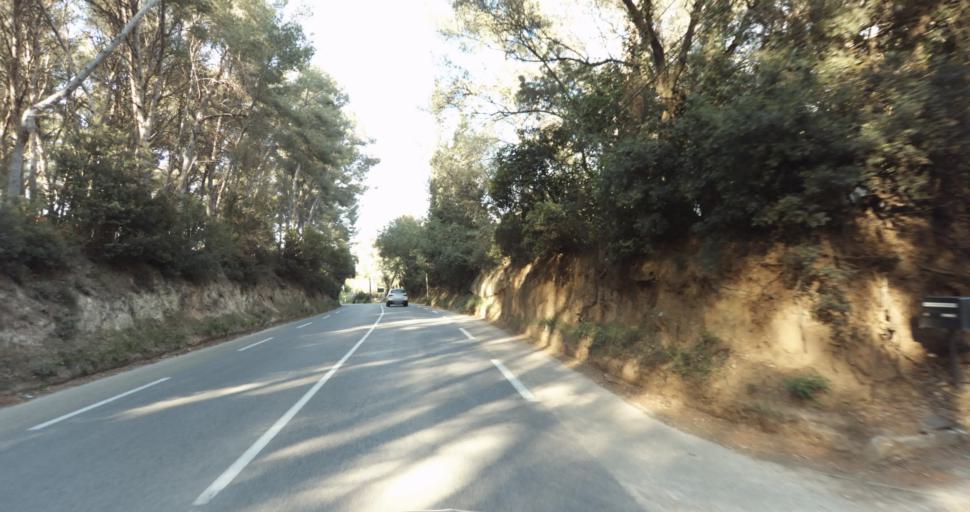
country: FR
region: Provence-Alpes-Cote d'Azur
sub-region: Departement du Var
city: Carqueiranne
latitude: 43.1138
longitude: 6.0553
